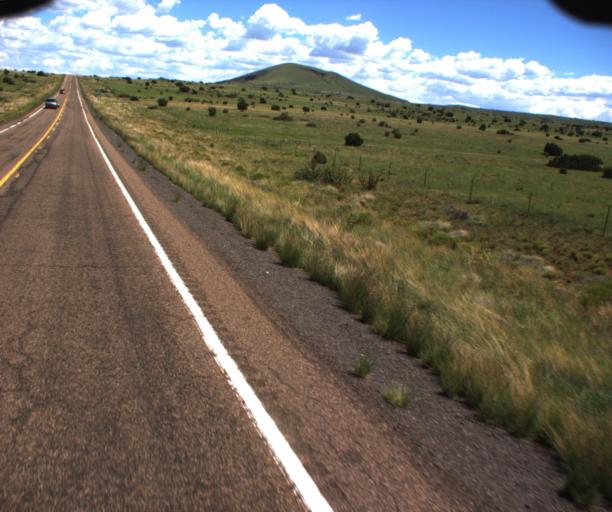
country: US
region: Arizona
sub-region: Apache County
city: Springerville
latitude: 34.2480
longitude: -109.5322
